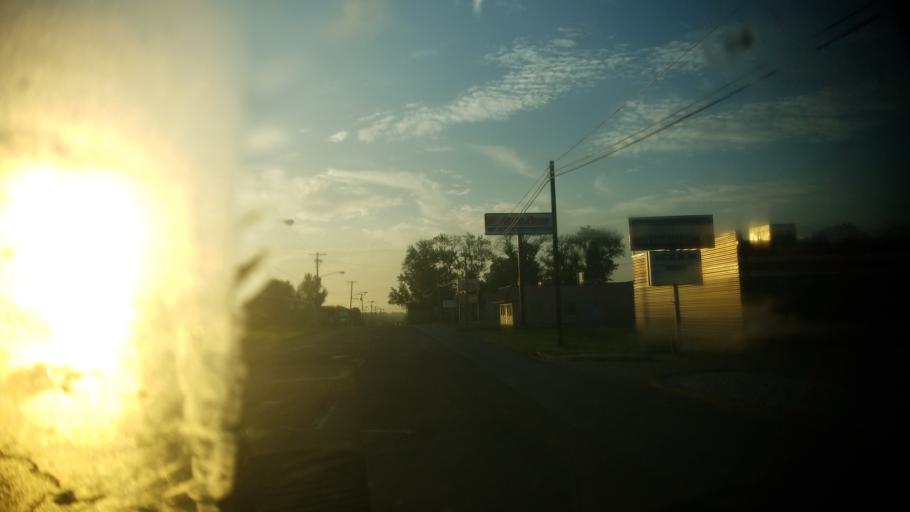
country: US
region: Illinois
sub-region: Wayne County
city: Fairfield
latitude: 38.3797
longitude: -88.3758
